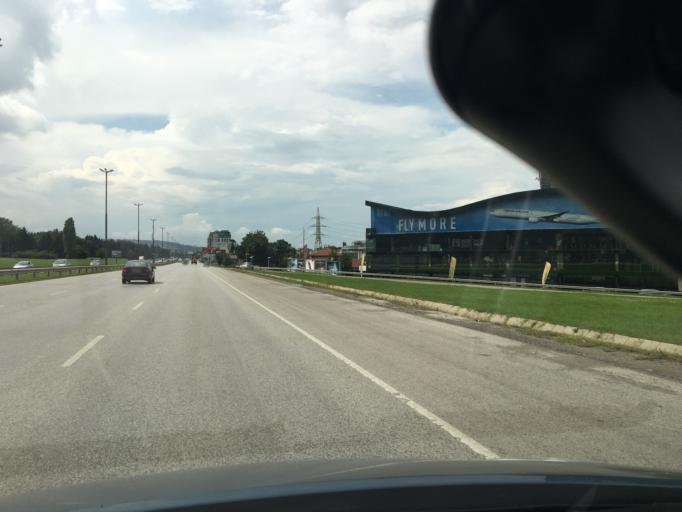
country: BG
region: Sofia-Capital
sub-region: Stolichna Obshtina
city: Sofia
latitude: 42.6544
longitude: 23.2813
